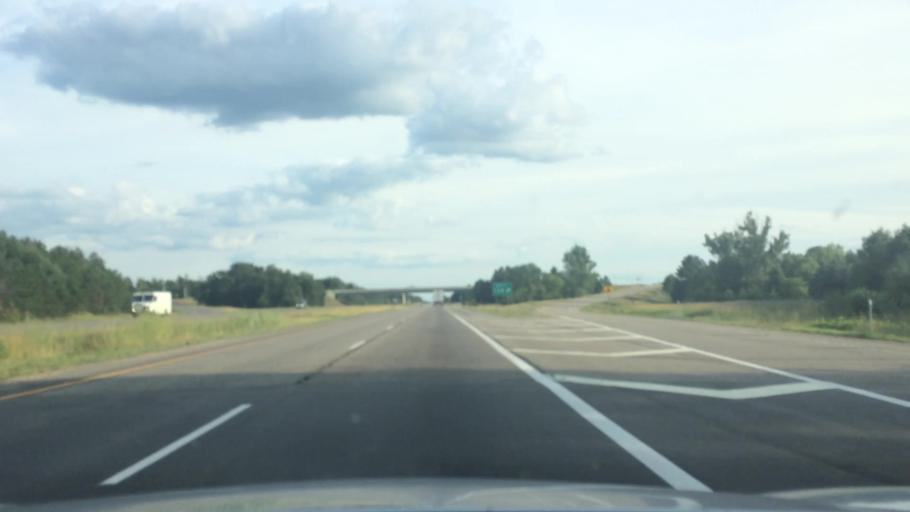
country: US
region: Wisconsin
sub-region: Portage County
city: Plover
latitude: 44.2626
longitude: -89.5240
